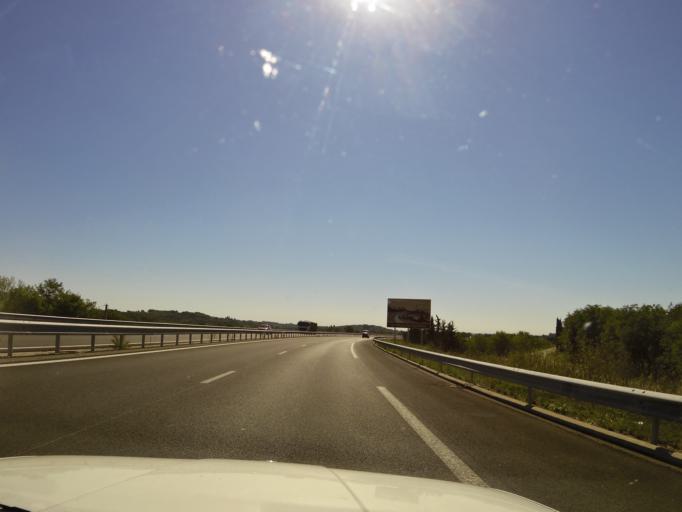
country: FR
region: Languedoc-Roussillon
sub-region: Departement du Gard
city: Vezenobres
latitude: 44.0111
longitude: 4.1706
